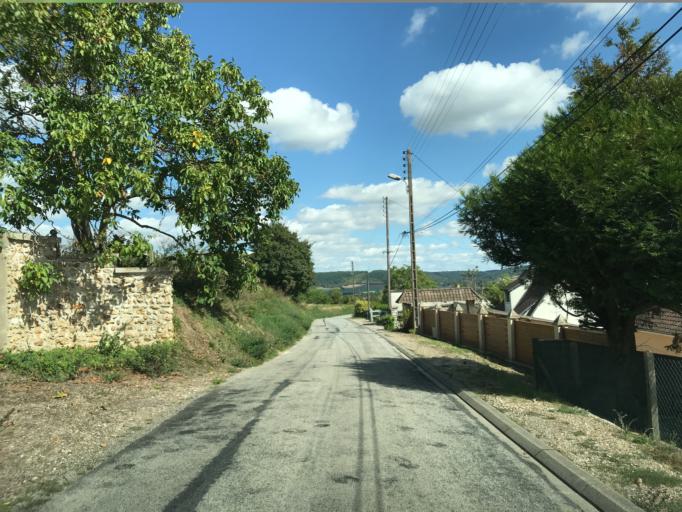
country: FR
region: Haute-Normandie
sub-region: Departement de l'Eure
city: Saint-Just
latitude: 49.1407
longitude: 1.4058
